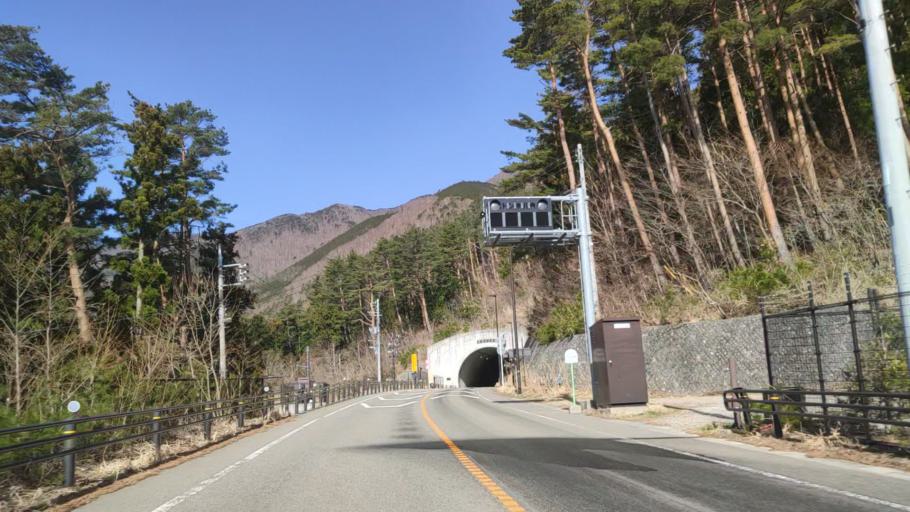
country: JP
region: Yamanashi
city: Fujikawaguchiko
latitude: 35.5279
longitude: 138.7163
